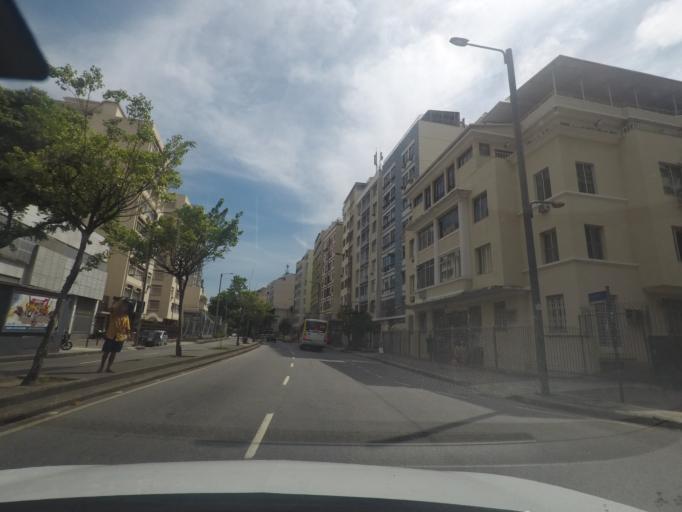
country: BR
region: Rio de Janeiro
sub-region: Rio De Janeiro
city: Rio de Janeiro
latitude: -22.9309
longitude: -43.2382
